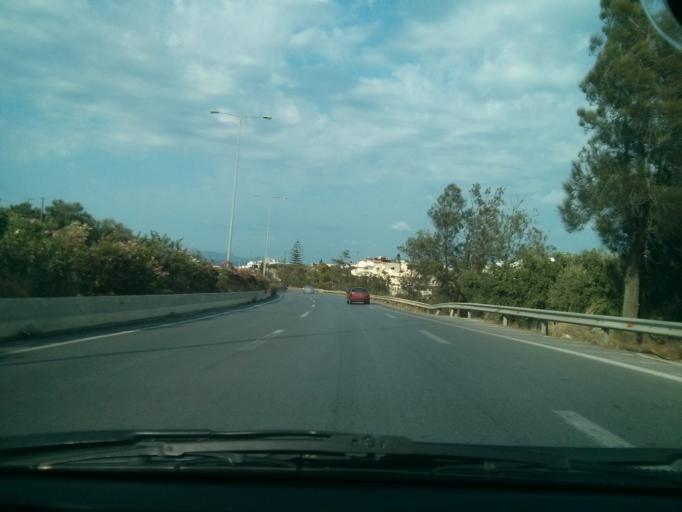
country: GR
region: Crete
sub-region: Nomos Irakleiou
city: Irakleion
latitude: 35.3225
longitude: 25.1489
